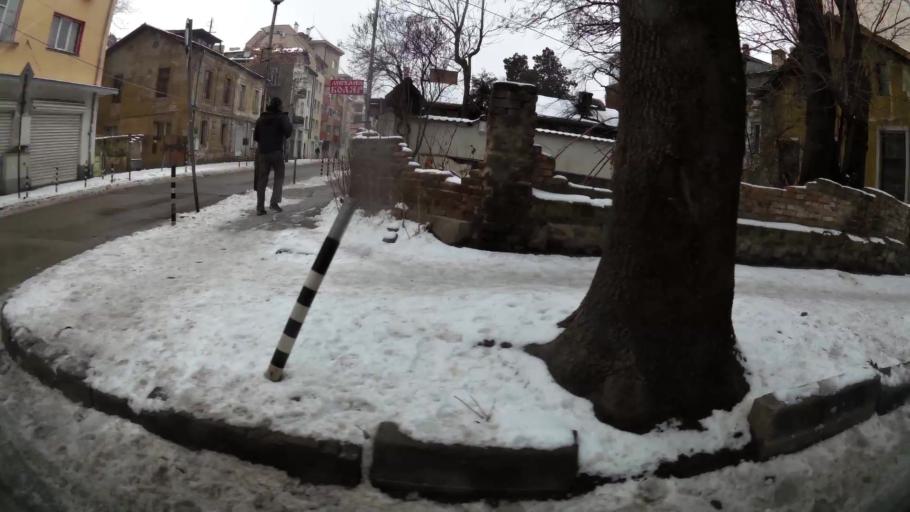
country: BG
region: Sofia-Capital
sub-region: Stolichna Obshtina
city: Sofia
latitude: 42.7066
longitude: 23.3219
